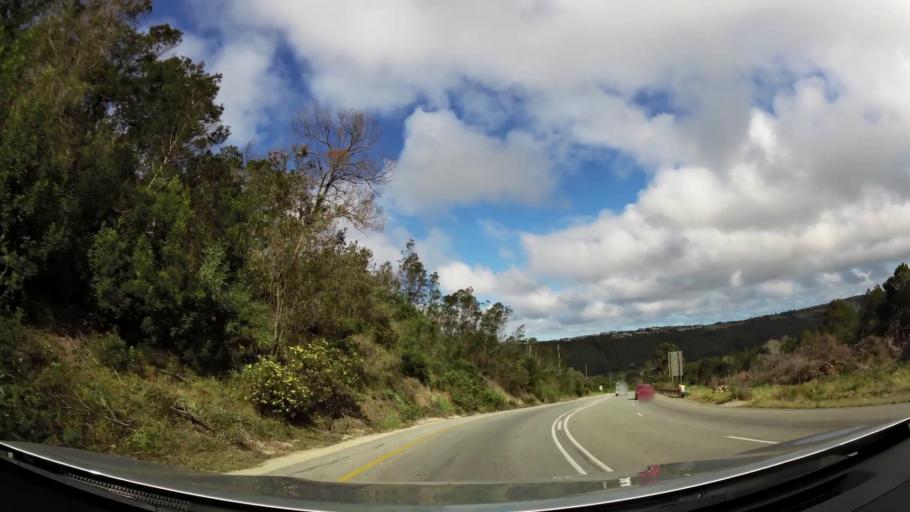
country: ZA
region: Western Cape
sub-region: Eden District Municipality
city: Plettenberg Bay
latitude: -34.0550
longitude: 23.3547
